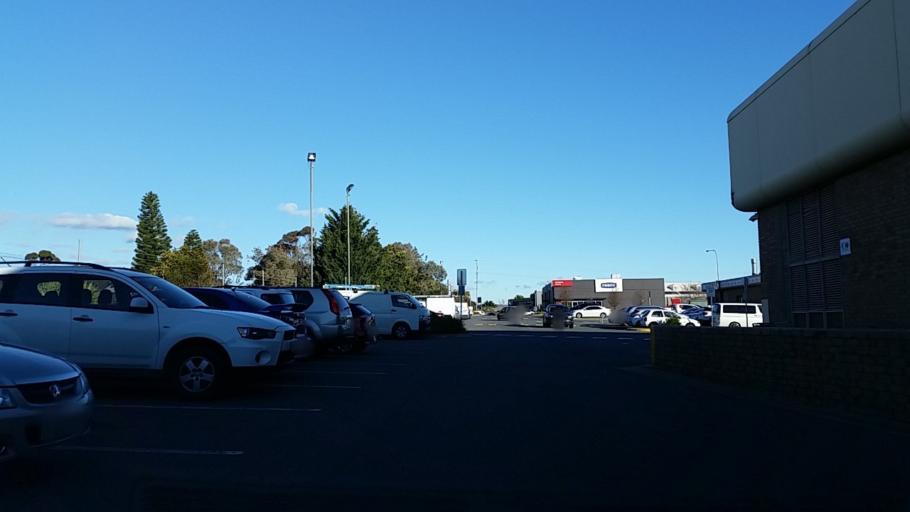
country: AU
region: South Australia
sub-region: Onkaparinga
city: Seaford
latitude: -35.1901
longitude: 138.4800
